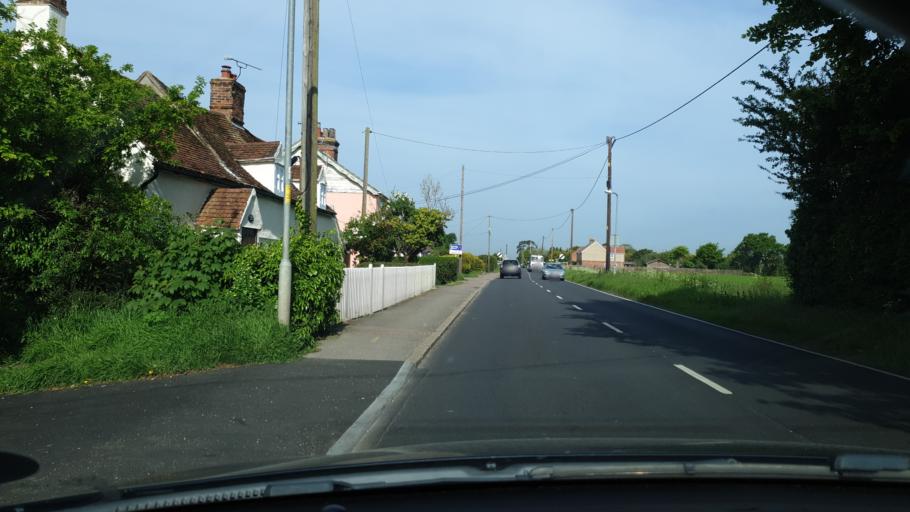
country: GB
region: England
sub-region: Essex
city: Frinton-on-Sea
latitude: 51.8455
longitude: 1.2006
